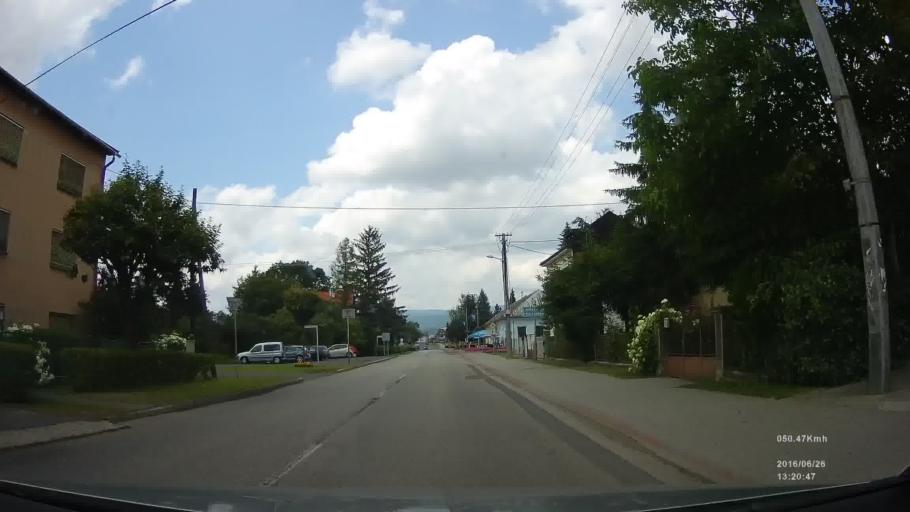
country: SK
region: Banskobystricky
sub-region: Okres Banska Bystrica
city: Zvolen
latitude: 48.6134
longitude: 19.1447
